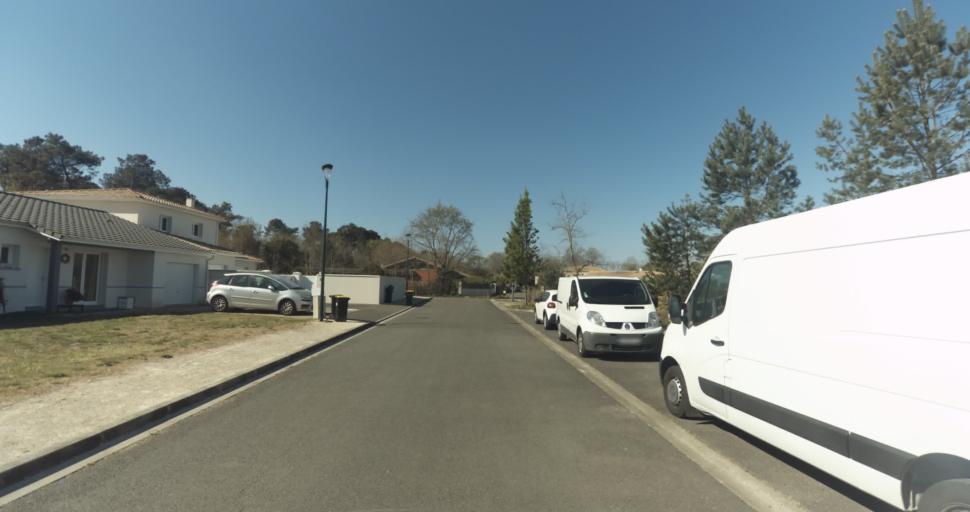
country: FR
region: Aquitaine
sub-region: Departement de la Gironde
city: Martignas-sur-Jalle
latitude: 44.7957
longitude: -0.8361
